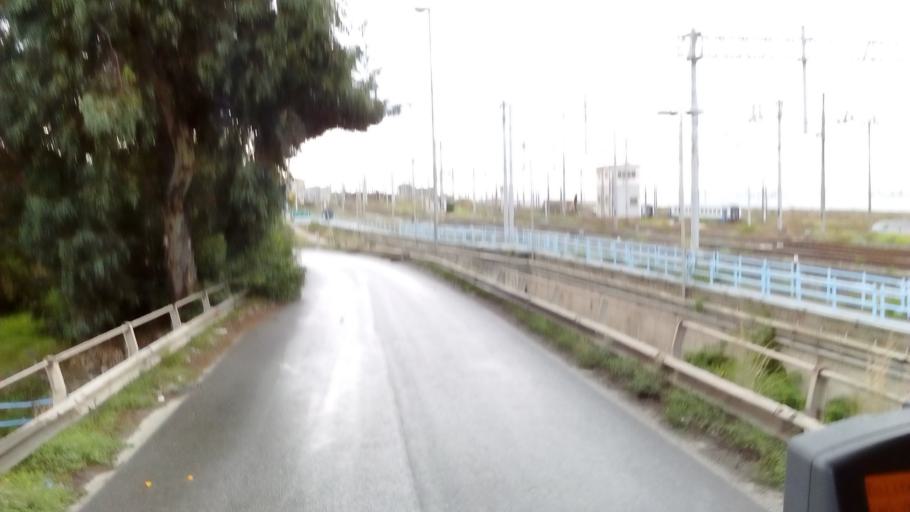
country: IT
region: Calabria
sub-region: Provincia di Reggio Calabria
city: Campo Calabro
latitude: 38.2151
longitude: 15.6348
